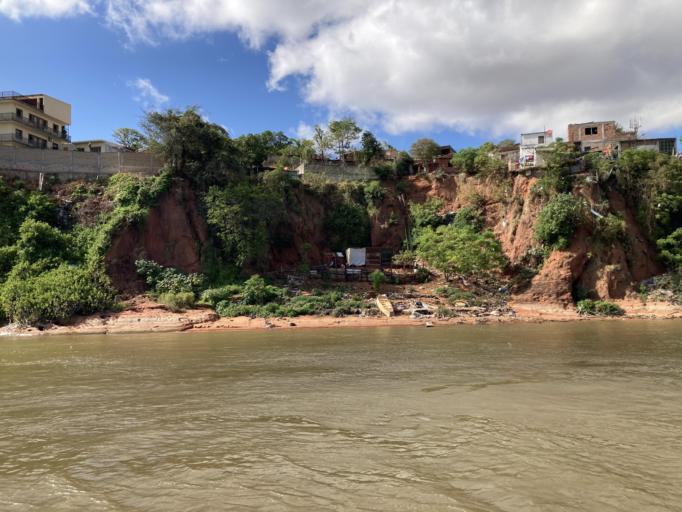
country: PY
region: Presidente Hayes
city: Nanawa
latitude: -25.2807
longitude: -57.6651
